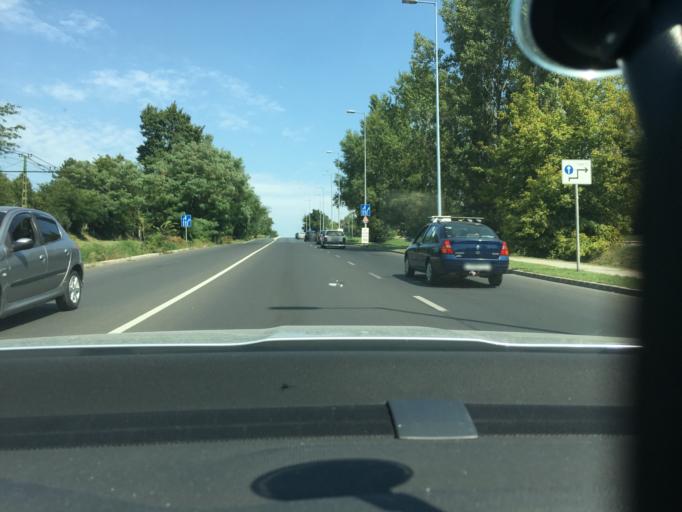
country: HU
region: Pest
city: Csomor
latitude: 47.5288
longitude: 19.2331
